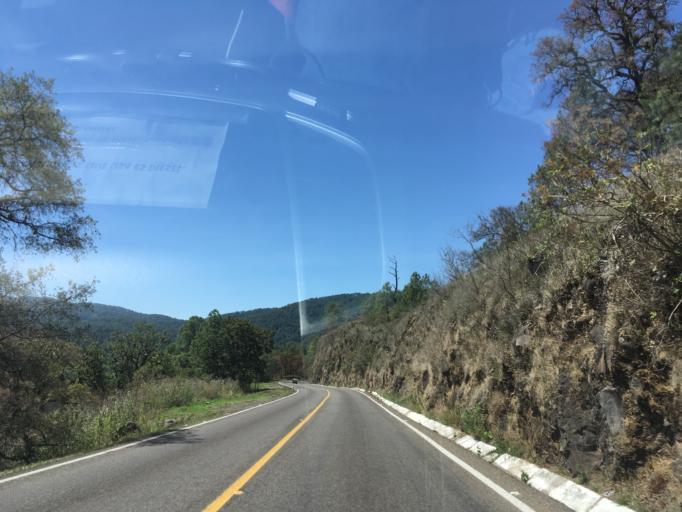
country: MX
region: Michoacan
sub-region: Hidalgo
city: Tierras Coloradas (San Pedro)
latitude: 19.6687
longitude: -100.7212
